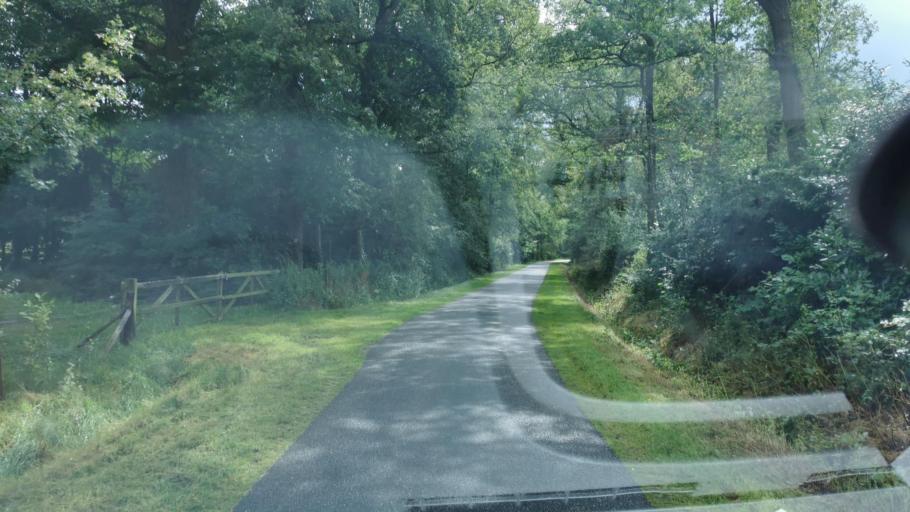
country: NL
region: Overijssel
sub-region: Gemeente Haaksbergen
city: Haaksbergen
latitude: 52.1422
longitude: 6.7230
